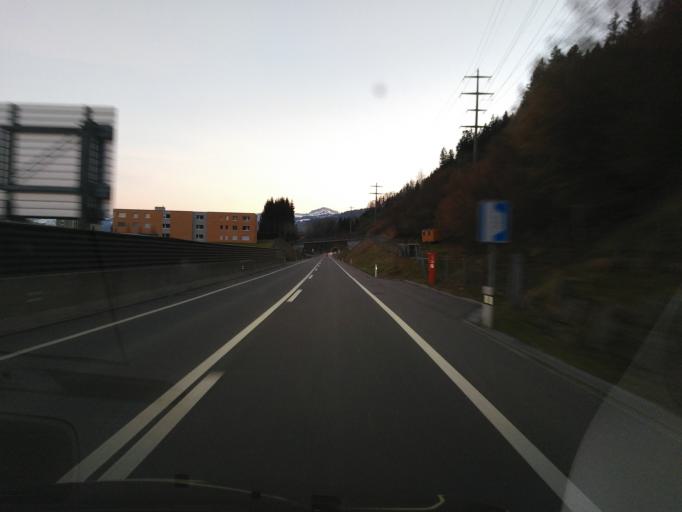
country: CH
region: Saint Gallen
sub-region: Wahlkreis Toggenburg
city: Wattwil
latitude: 47.3088
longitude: 9.0777
